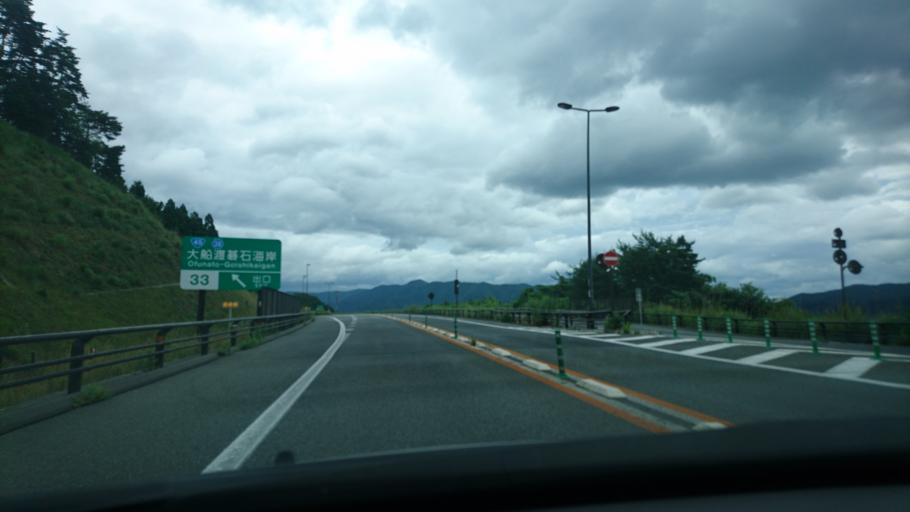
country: JP
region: Iwate
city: Ofunato
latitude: 39.0311
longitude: 141.7098
